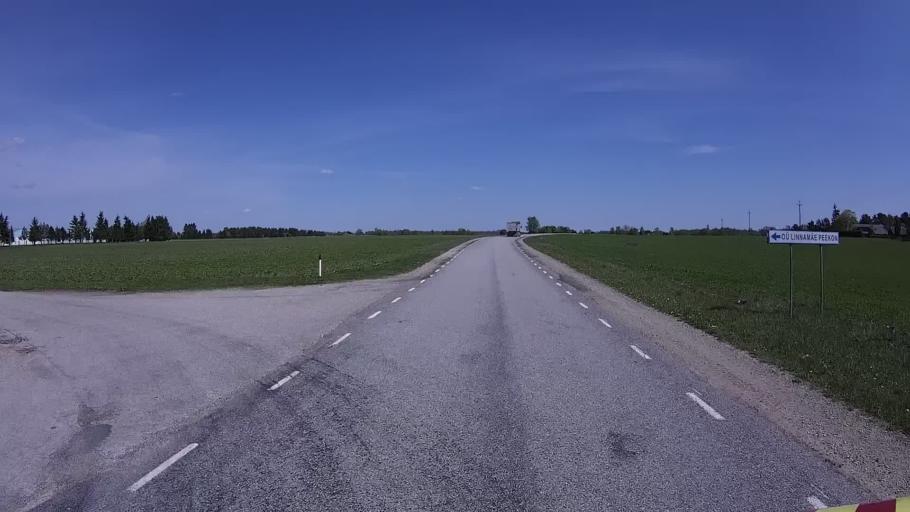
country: EE
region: Laeaene
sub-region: Ridala Parish
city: Uuemoisa
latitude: 59.0014
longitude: 23.7362
